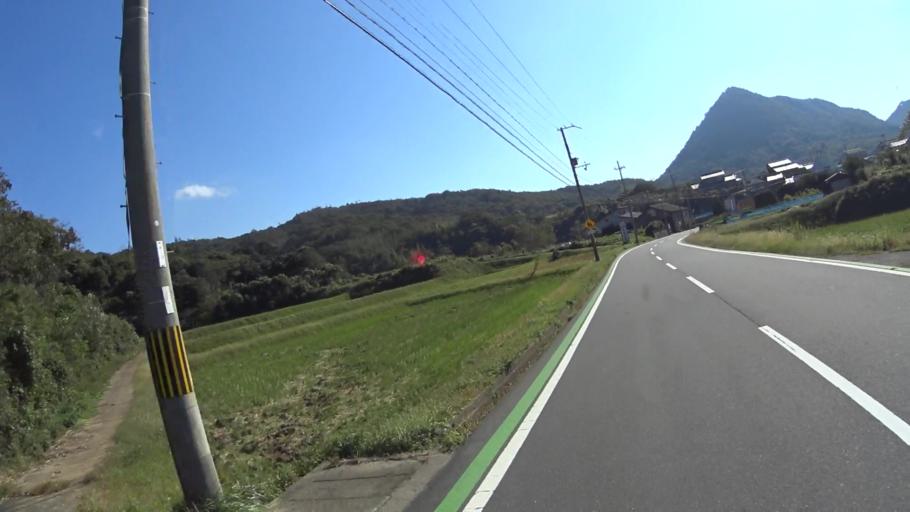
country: JP
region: Kyoto
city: Miyazu
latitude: 35.7226
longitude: 135.0838
